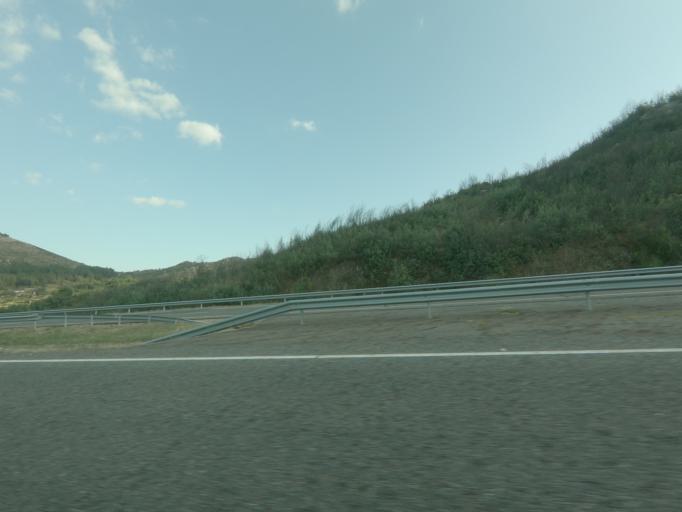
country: ES
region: Galicia
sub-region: Provincia de Ourense
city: Oimbra
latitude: 41.9230
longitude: -7.4796
